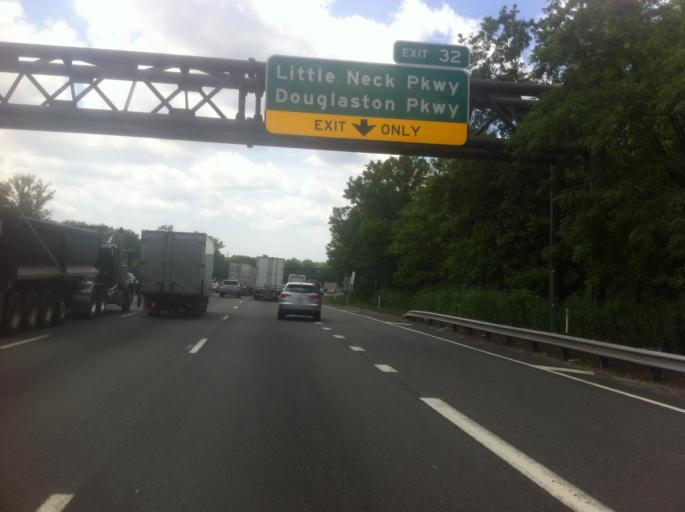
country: US
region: New York
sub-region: Nassau County
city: Lake Success
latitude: 40.7683
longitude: -73.7019
